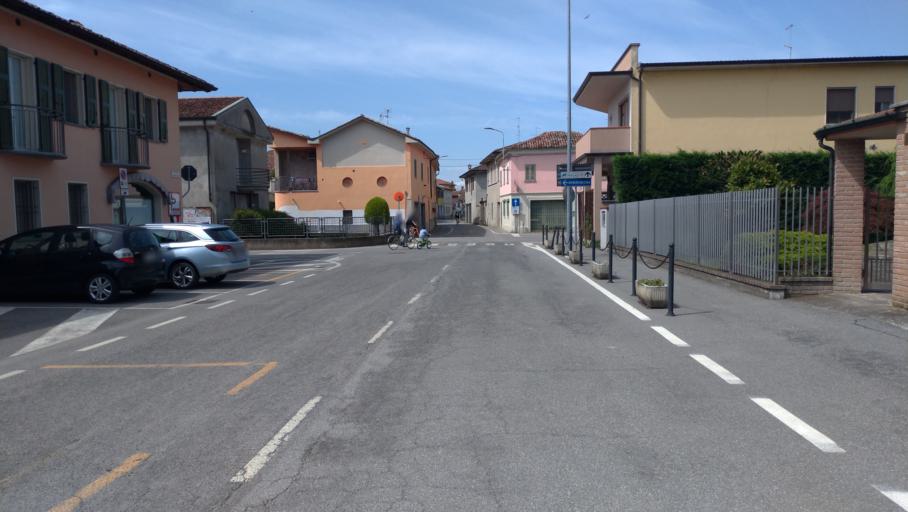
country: IT
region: Lombardy
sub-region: Provincia di Cremona
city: Madignano
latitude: 45.3429
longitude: 9.7257
